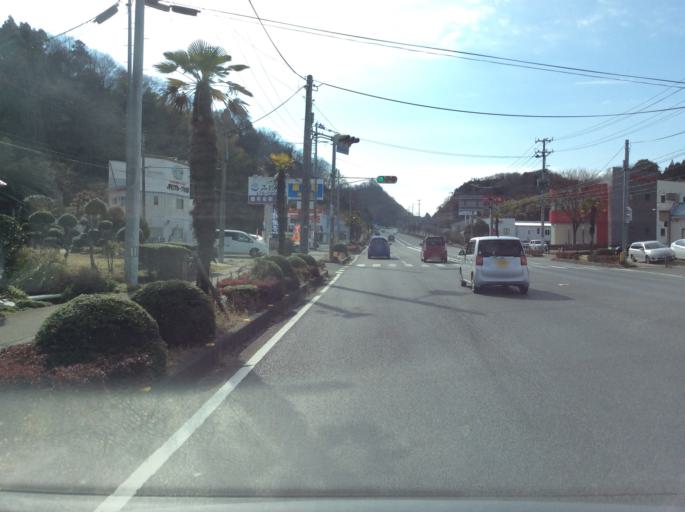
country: JP
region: Fukushima
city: Iwaki
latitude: 36.9806
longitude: 140.9010
